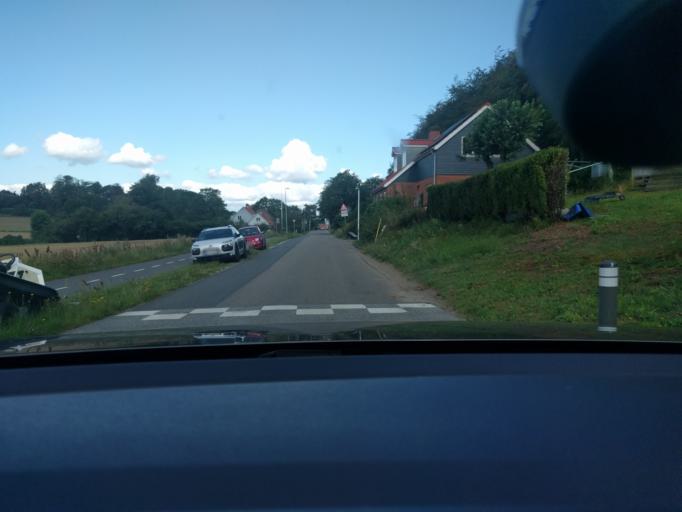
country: DK
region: Central Jutland
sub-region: Viborg Kommune
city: Viborg
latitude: 56.5267
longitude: 9.3252
